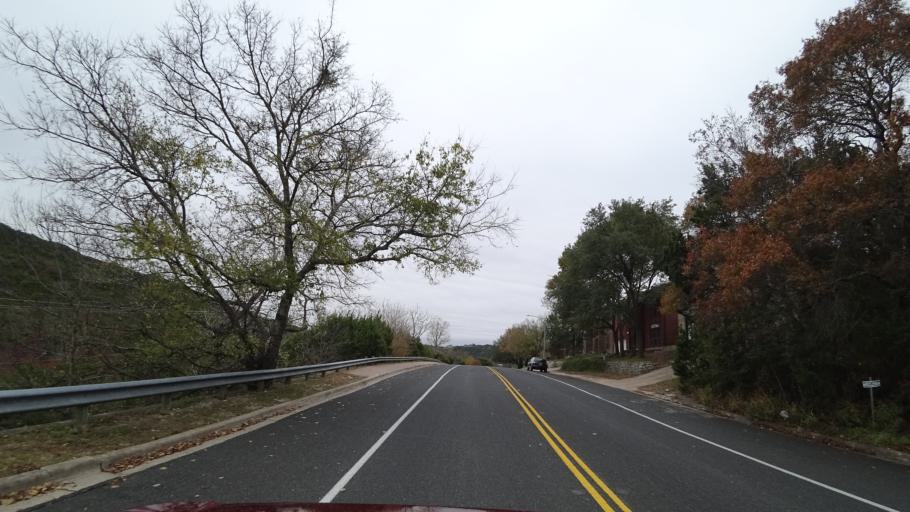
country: US
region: Texas
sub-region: Williamson County
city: Jollyville
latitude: 30.3823
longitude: -97.7881
